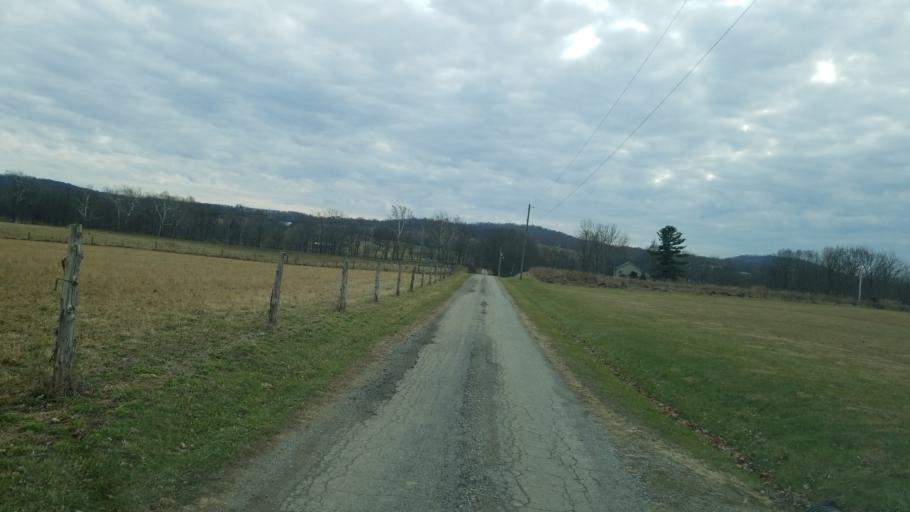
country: US
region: Ohio
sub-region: Highland County
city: Greenfield
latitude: 39.3272
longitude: -83.3264
